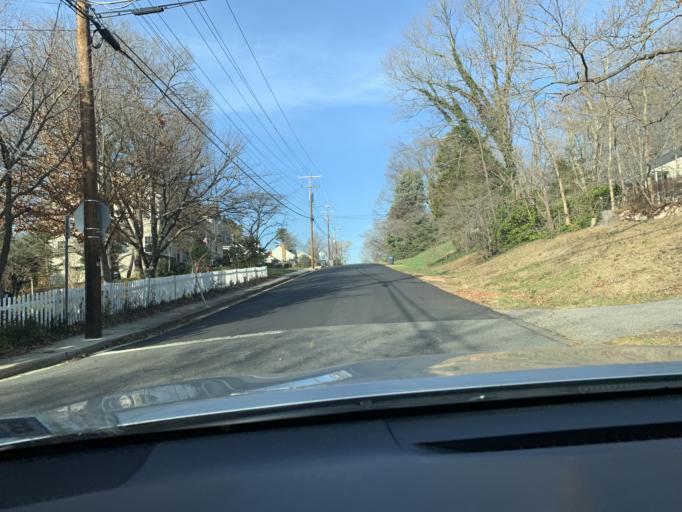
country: US
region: Virginia
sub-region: Fairfax County
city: Jefferson
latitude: 38.8538
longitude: -77.1849
